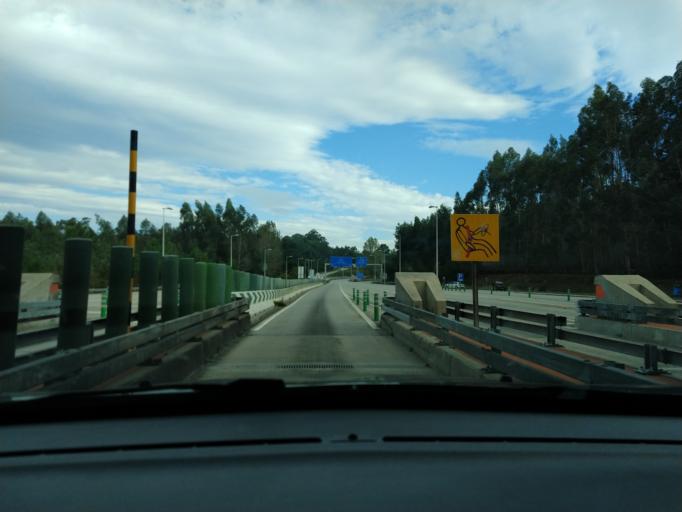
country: PT
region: Aveiro
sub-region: Albergaria-A-Velha
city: Albergaria-a-Velha
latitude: 40.6892
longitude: -8.5246
